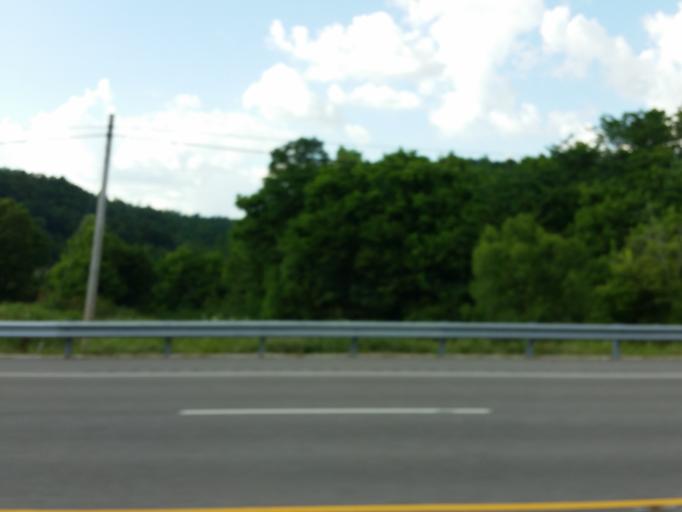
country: US
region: Tennessee
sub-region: Lewis County
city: Hohenwald
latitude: 35.5672
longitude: -87.4143
